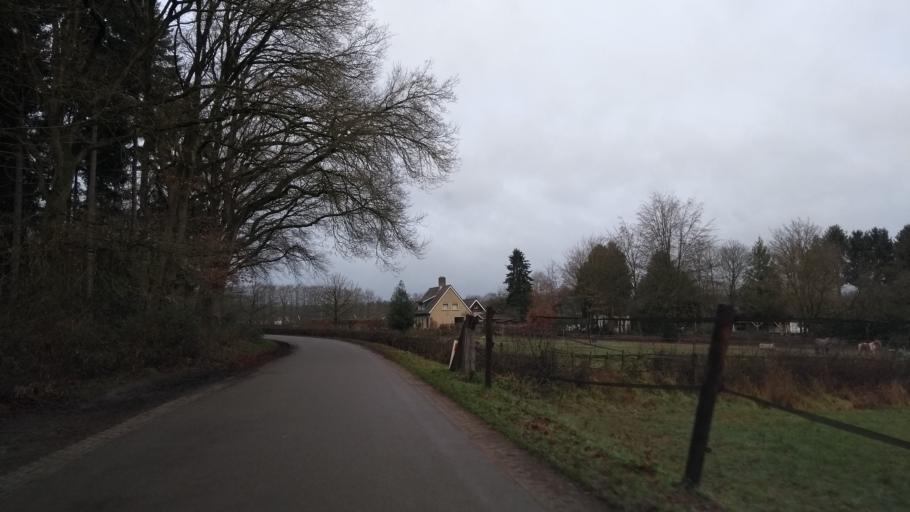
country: NL
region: Gelderland
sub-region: Gemeente Rheden
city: Dieren
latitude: 52.0670
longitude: 6.0857
